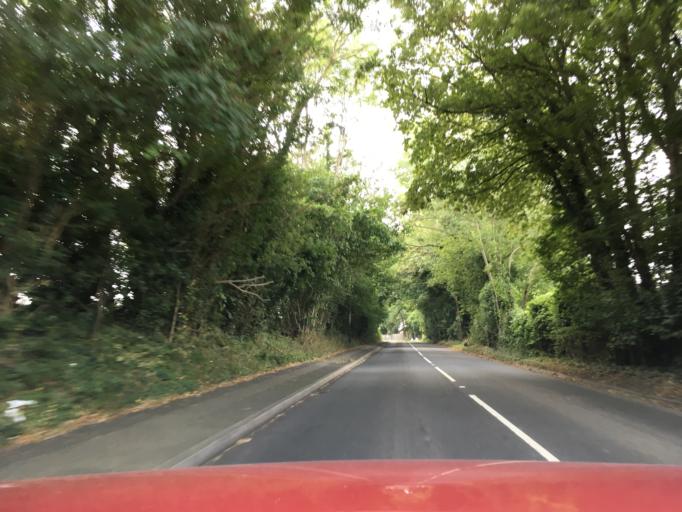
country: GB
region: England
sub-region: Kent
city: Kings Hill
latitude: 51.2835
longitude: 0.3974
